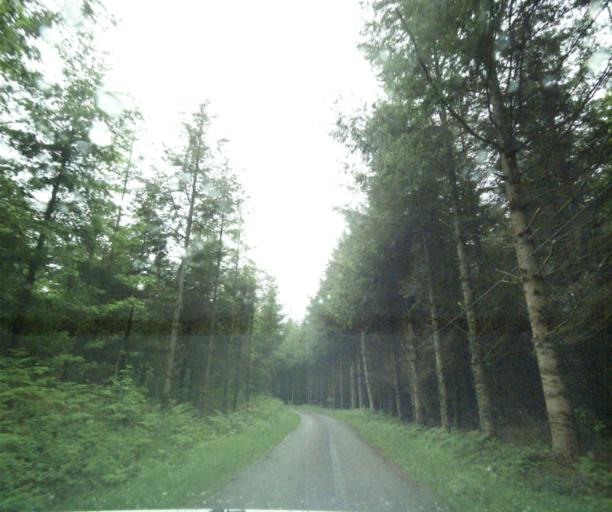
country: FR
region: Bourgogne
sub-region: Departement de Saone-et-Loire
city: La Clayette
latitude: 46.3706
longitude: 4.3665
